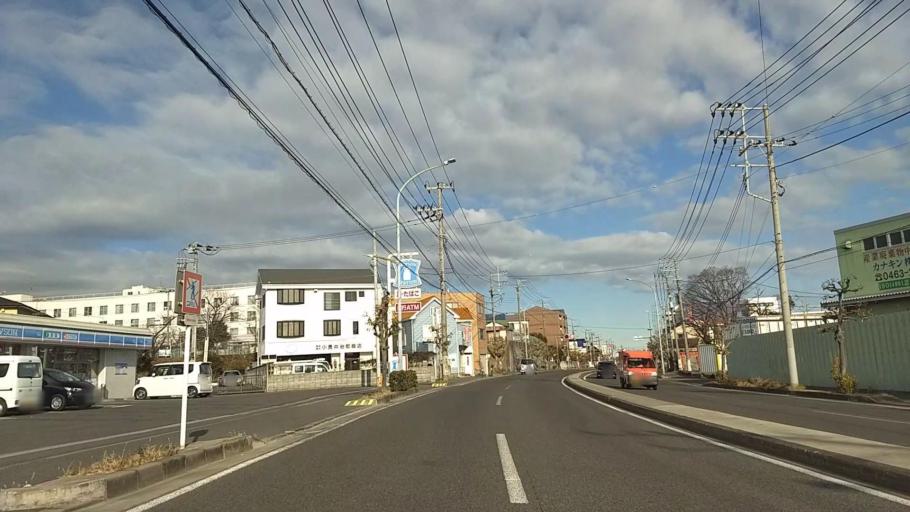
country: JP
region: Kanagawa
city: Hiratsuka
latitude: 35.3407
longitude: 139.3564
